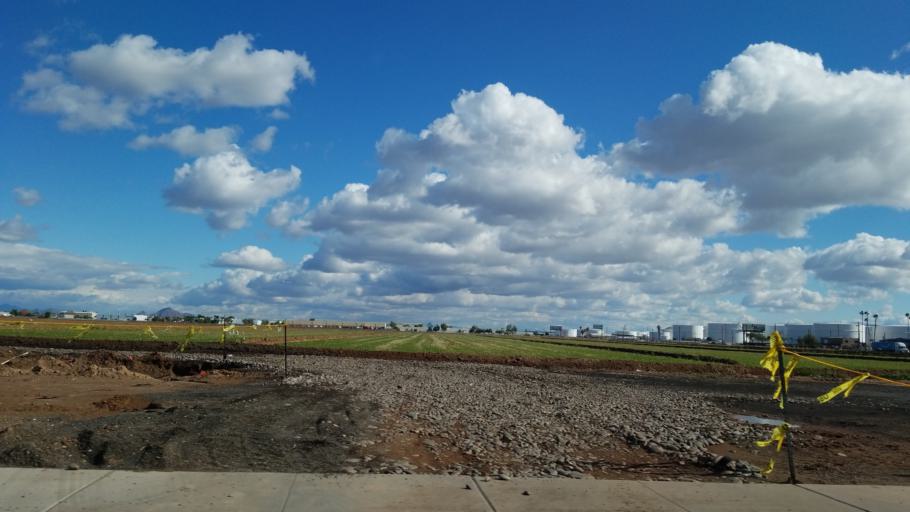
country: US
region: Arizona
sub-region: Maricopa County
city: Tolleson
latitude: 33.4531
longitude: -112.1852
